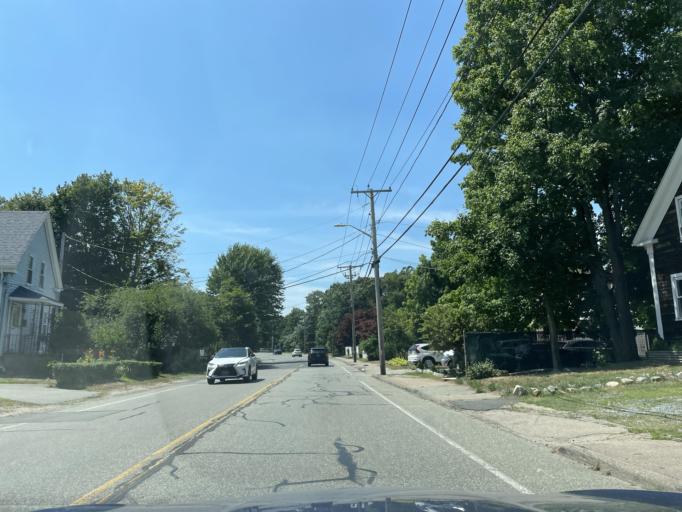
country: US
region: Massachusetts
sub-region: Norfolk County
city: Randolph
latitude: 42.1653
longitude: -71.0531
